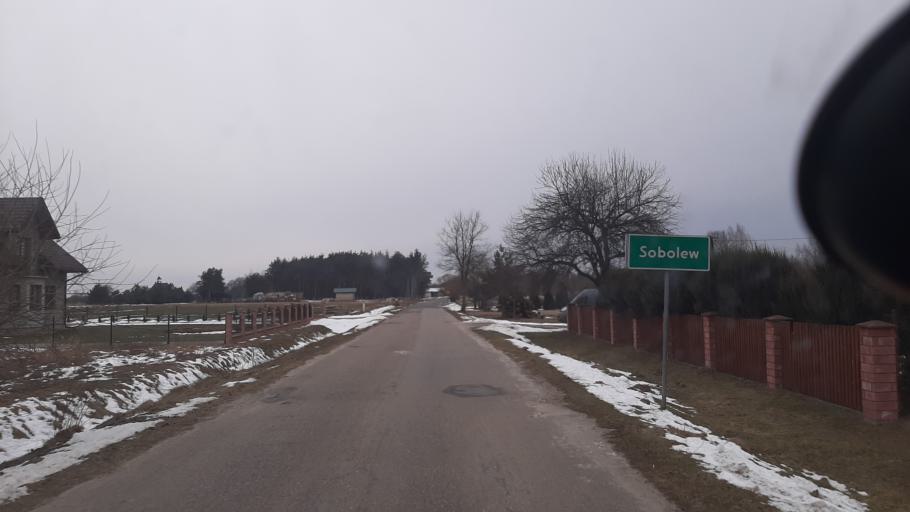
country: PL
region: Lublin Voivodeship
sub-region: Powiat lubartowski
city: Kamionka
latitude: 51.5160
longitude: 22.4826
